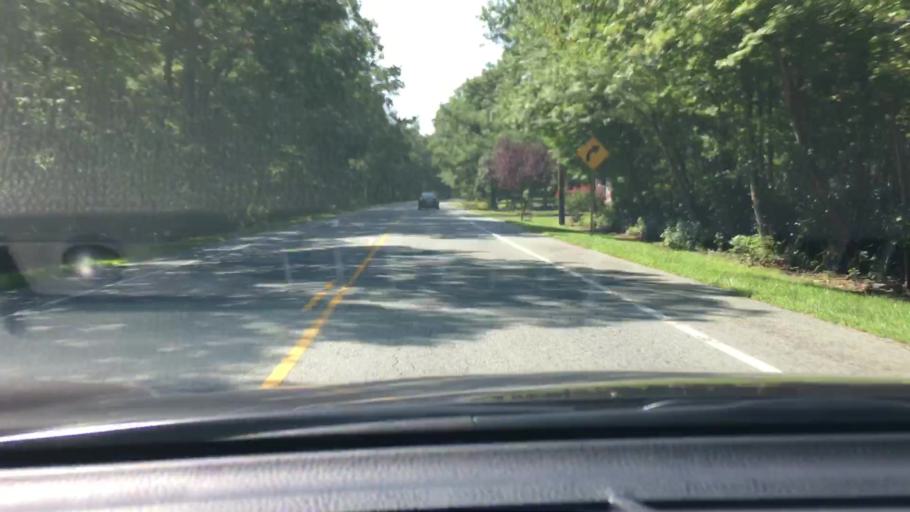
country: US
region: New Jersey
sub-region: Cape May County
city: Woodbine
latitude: 39.2544
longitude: -74.8059
